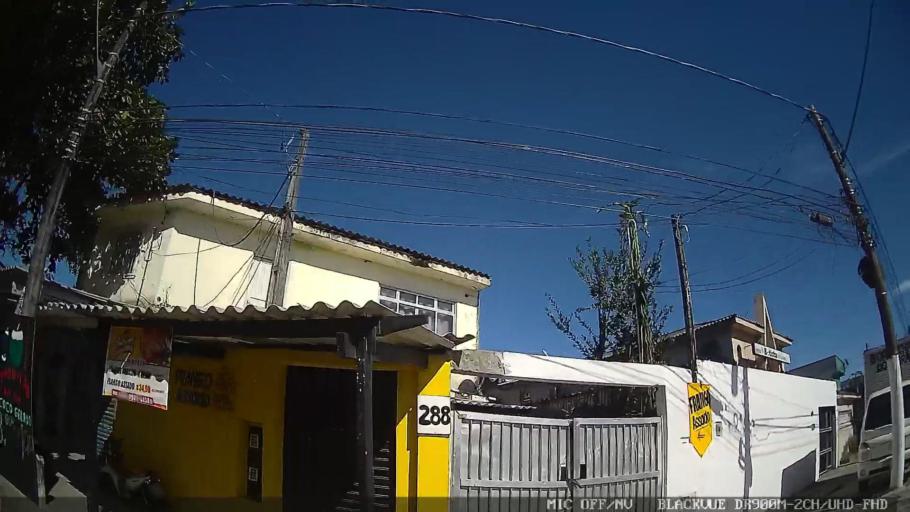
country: BR
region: Sao Paulo
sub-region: Santos
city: Santos
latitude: -23.9436
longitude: -46.2825
